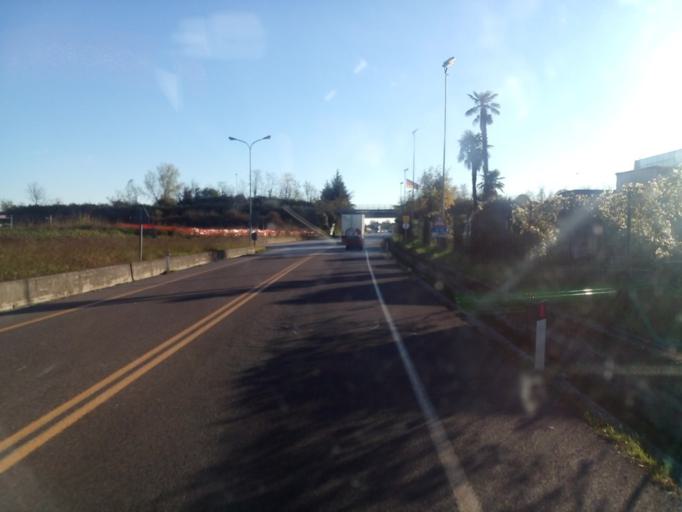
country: IT
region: Veneto
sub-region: Provincia di Vicenza
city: Bassano del Grappa
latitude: 45.7384
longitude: 11.7294
